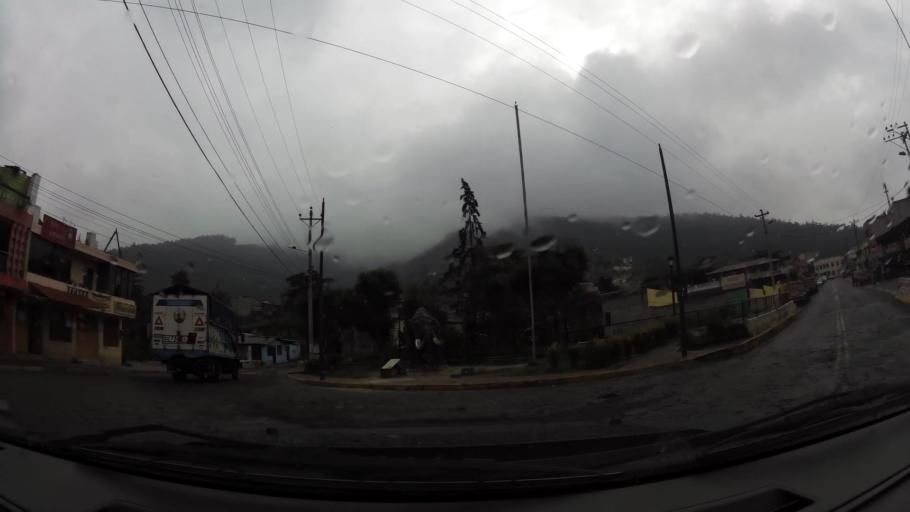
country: EC
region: Pichincha
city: Sangolqui
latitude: -0.2872
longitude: -78.4412
